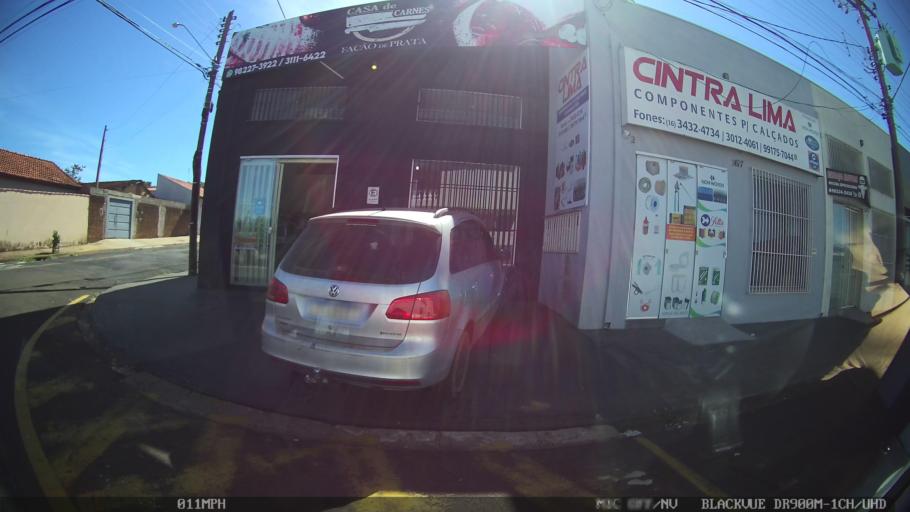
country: BR
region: Sao Paulo
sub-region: Franca
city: Franca
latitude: -20.5470
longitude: -47.3827
